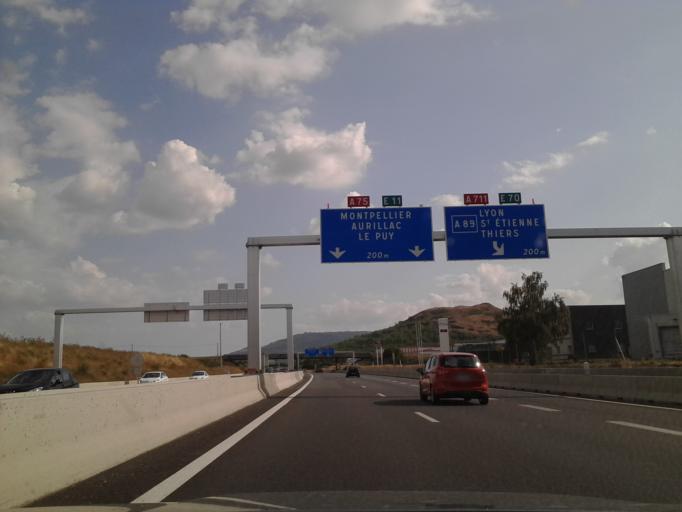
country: FR
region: Auvergne
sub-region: Departement du Puy-de-Dome
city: Aulnat
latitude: 45.7813
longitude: 3.1416
